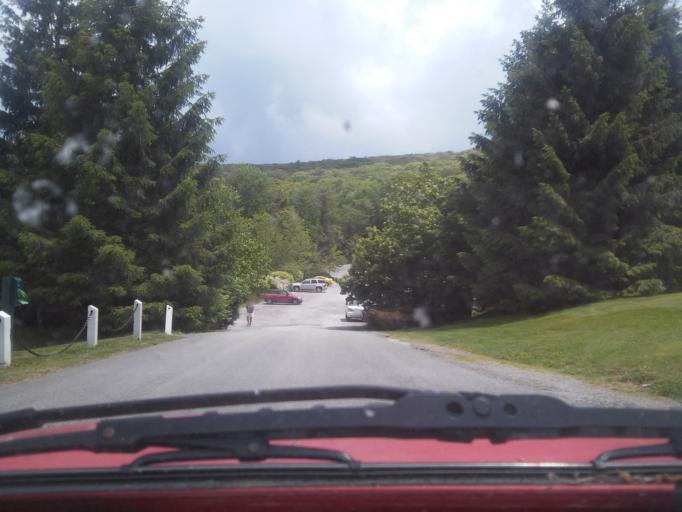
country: US
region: Virginia
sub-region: Giles County
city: Pembroke
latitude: 37.3555
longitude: -80.5368
